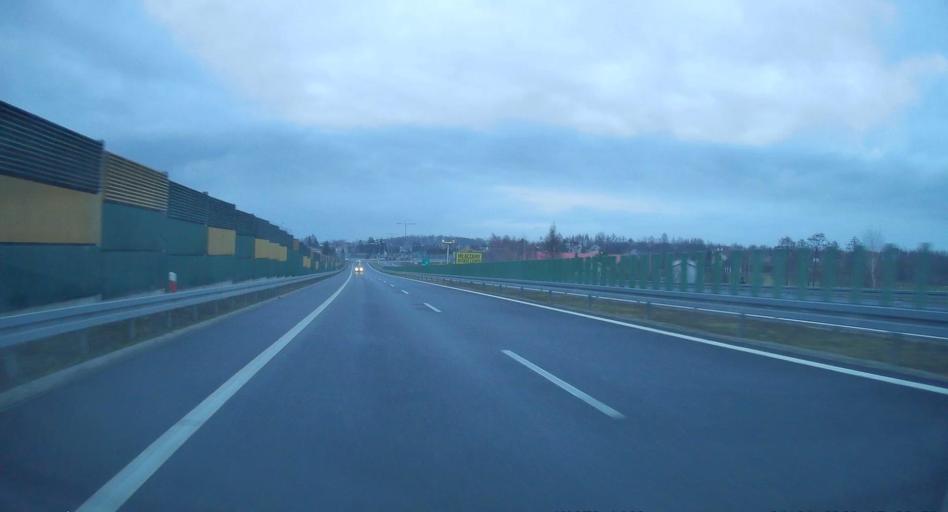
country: PL
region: Subcarpathian Voivodeship
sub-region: Powiat ropczycko-sedziszowski
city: Ropczyce
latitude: 50.0547
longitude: 21.6289
